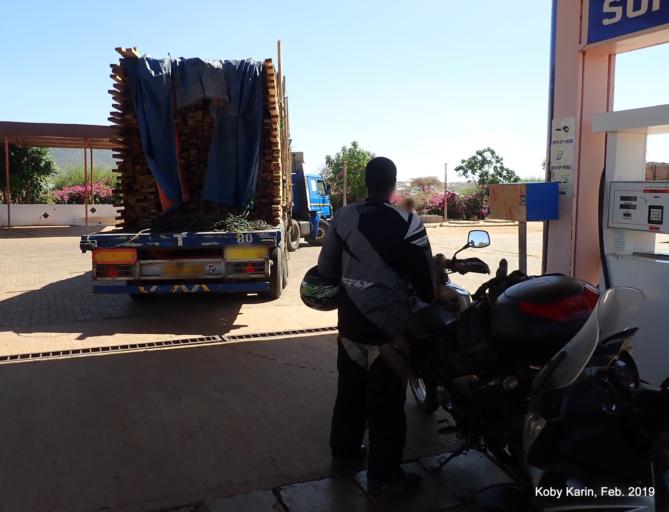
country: TZ
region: Arusha
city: Namanga
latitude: -2.5654
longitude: 36.7779
